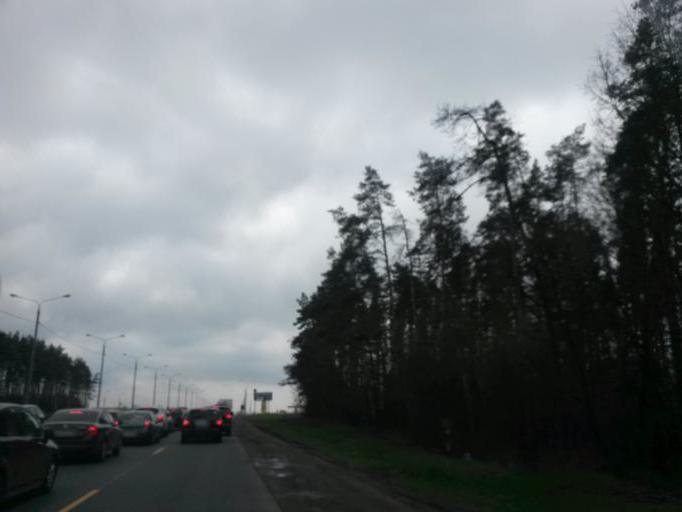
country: RU
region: Moskovskaya
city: Klimovsk
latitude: 55.3616
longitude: 37.5996
